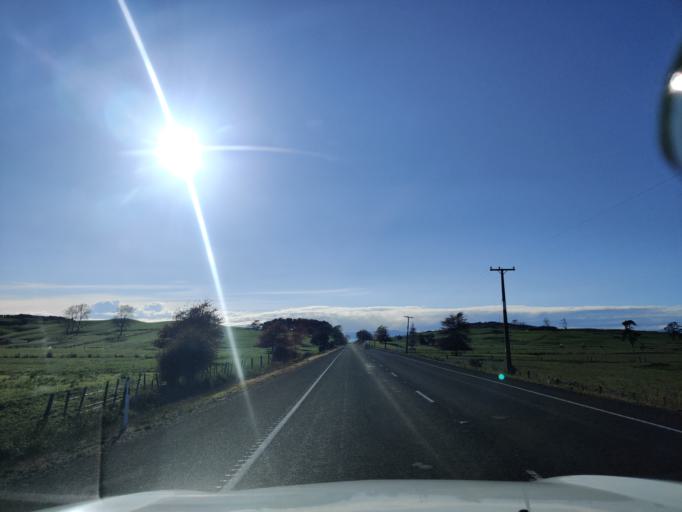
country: NZ
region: Waikato
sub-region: Hauraki District
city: Ngatea
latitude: -37.2868
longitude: 175.3908
